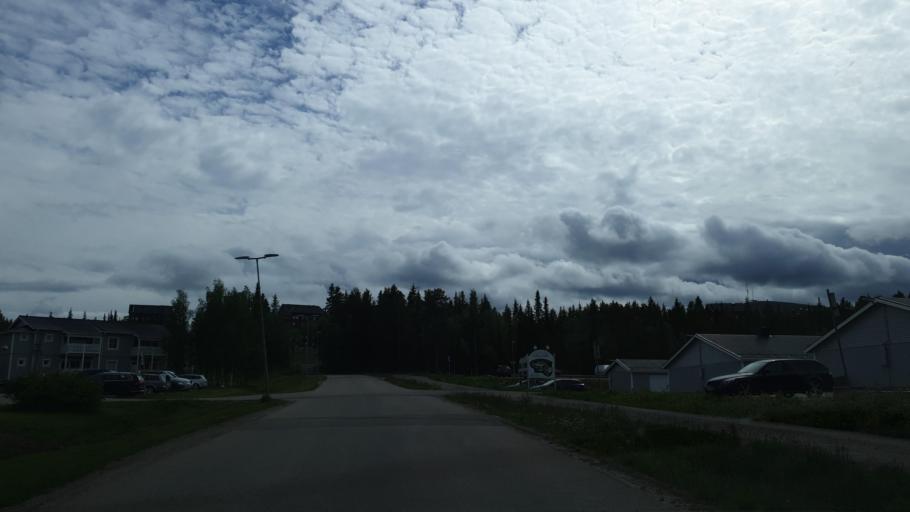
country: SE
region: Norrbotten
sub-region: Gallivare Kommun
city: Gaellivare
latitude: 67.1260
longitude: 20.6564
